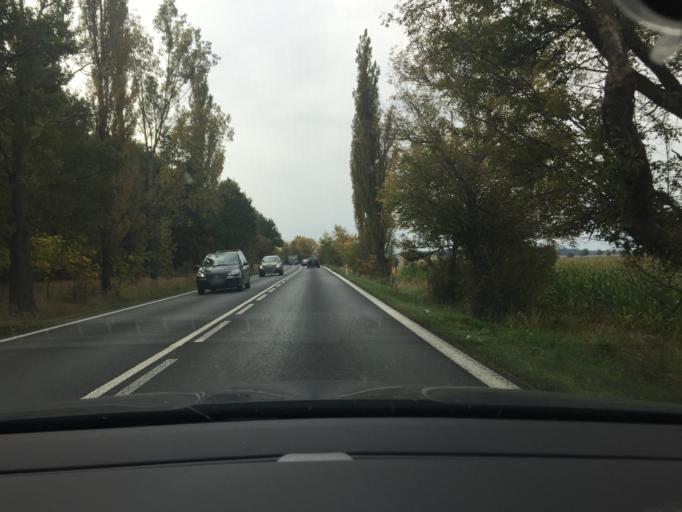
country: CZ
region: Central Bohemia
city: Milin
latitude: 49.5867
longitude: 14.0714
